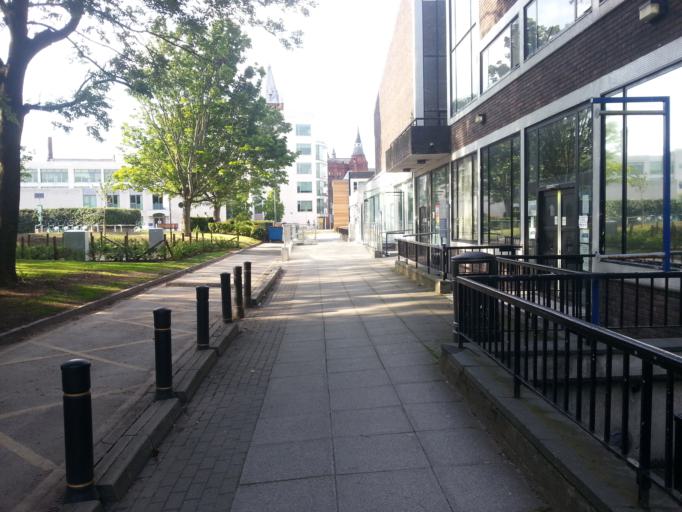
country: GB
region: England
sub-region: Liverpool
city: Liverpool
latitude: 53.4046
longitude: -2.9667
